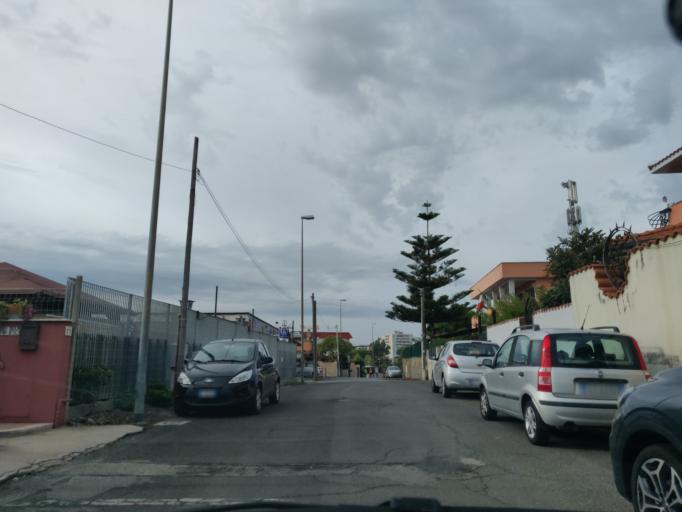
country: IT
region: Latium
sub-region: Citta metropolitana di Roma Capitale
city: Civitavecchia
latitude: 42.0750
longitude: 11.8103
